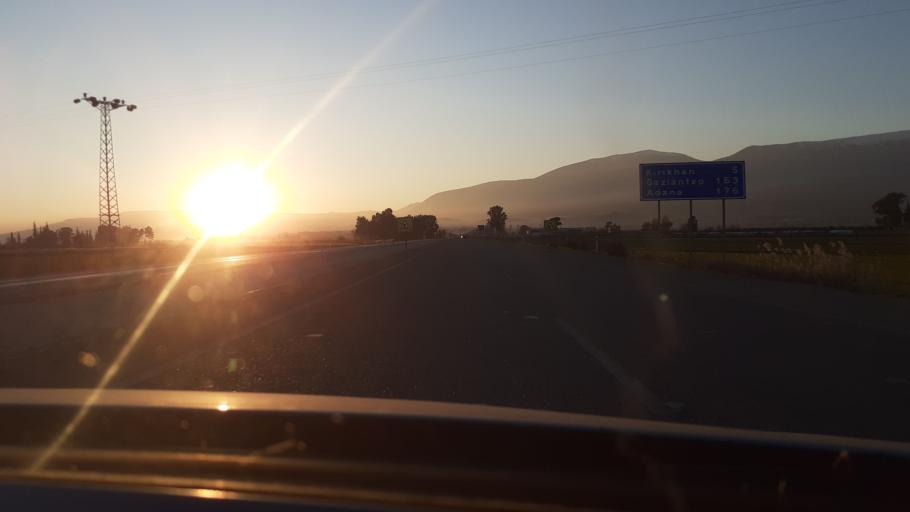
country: TR
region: Hatay
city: Kirikhan
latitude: 36.5060
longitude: 36.4217
